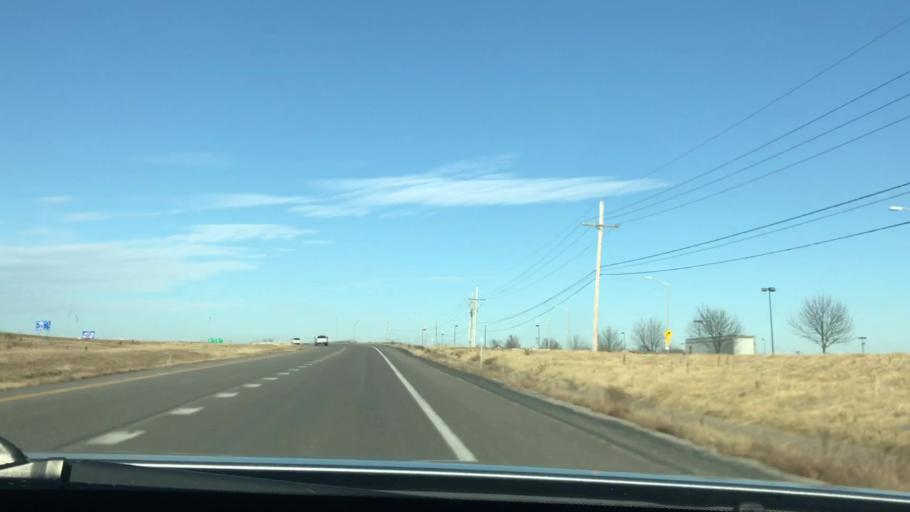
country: US
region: Missouri
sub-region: Platte County
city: Weatherby Lake
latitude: 39.2440
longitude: -94.6575
